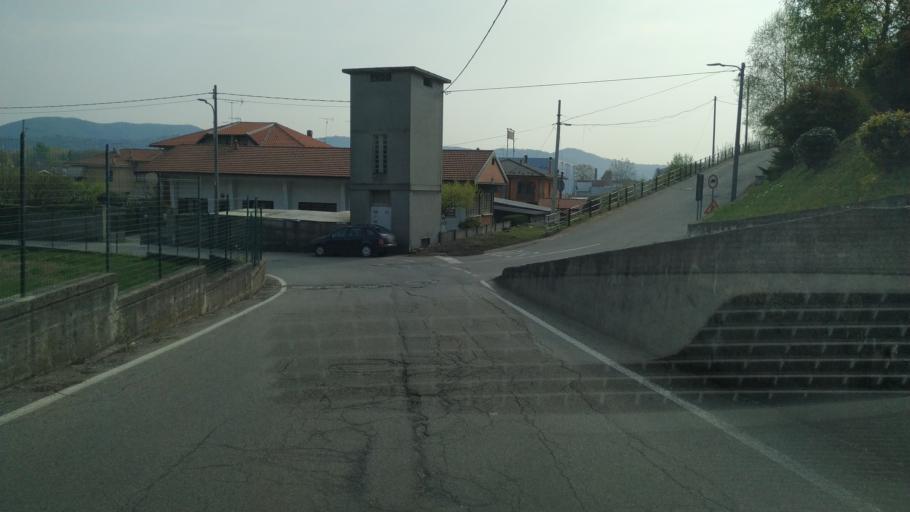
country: IT
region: Piedmont
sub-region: Provincia di Novara
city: San Maurizio D'Opaglio
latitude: 45.7714
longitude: 8.3907
